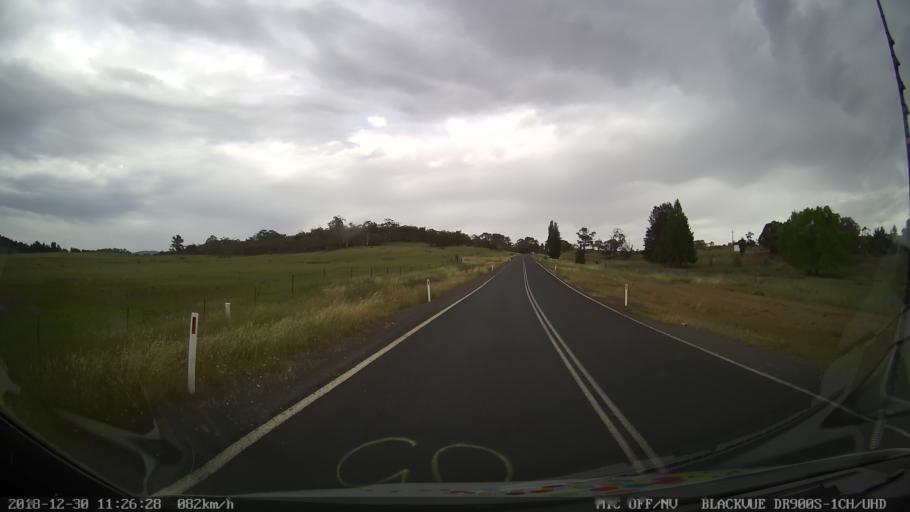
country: AU
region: New South Wales
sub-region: Snowy River
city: Jindabyne
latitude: -36.4682
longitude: 148.6336
